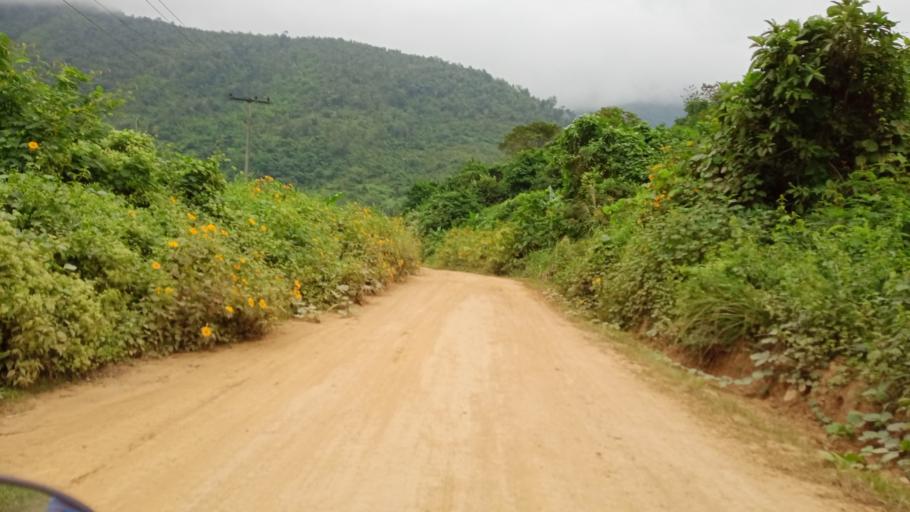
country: LA
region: Xiangkhoang
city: Phonsavan
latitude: 19.0934
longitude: 102.9876
